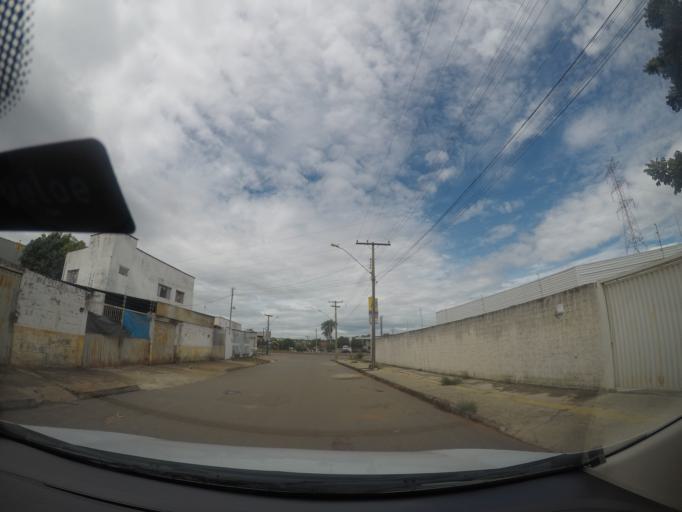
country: BR
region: Goias
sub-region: Goiania
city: Goiania
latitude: -16.7392
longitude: -49.3452
